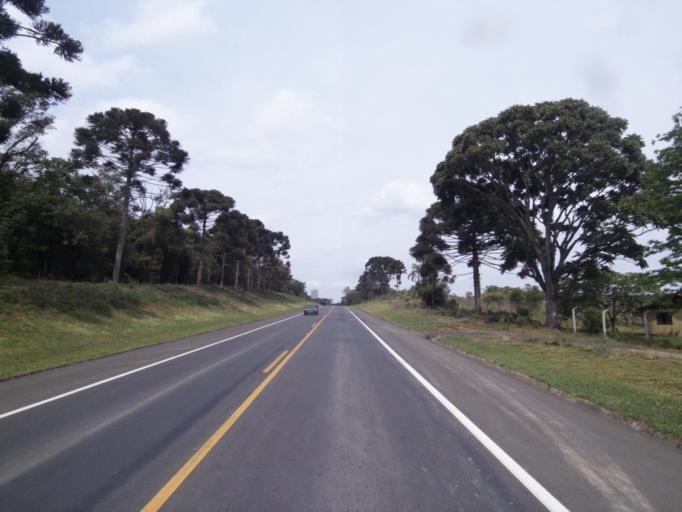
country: BR
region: Parana
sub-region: Irati
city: Irati
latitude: -25.4702
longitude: -50.5006
